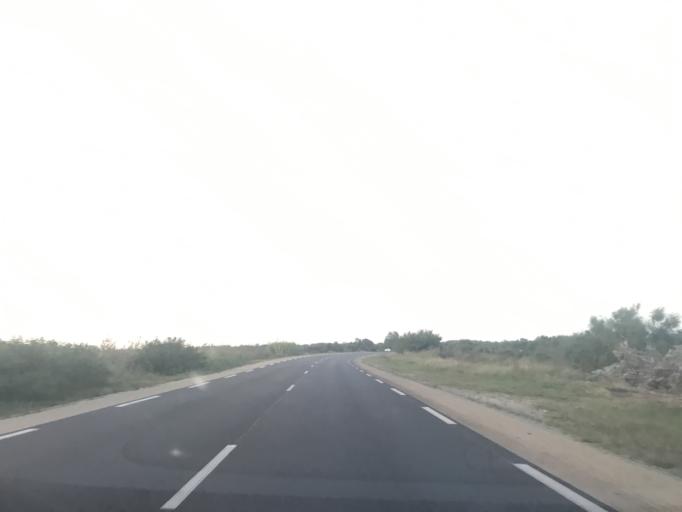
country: FR
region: Provence-Alpes-Cote d'Azur
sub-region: Departement des Bouches-du-Rhone
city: Saintes-Maries-de-la-Mer
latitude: 43.5374
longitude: 4.4005
